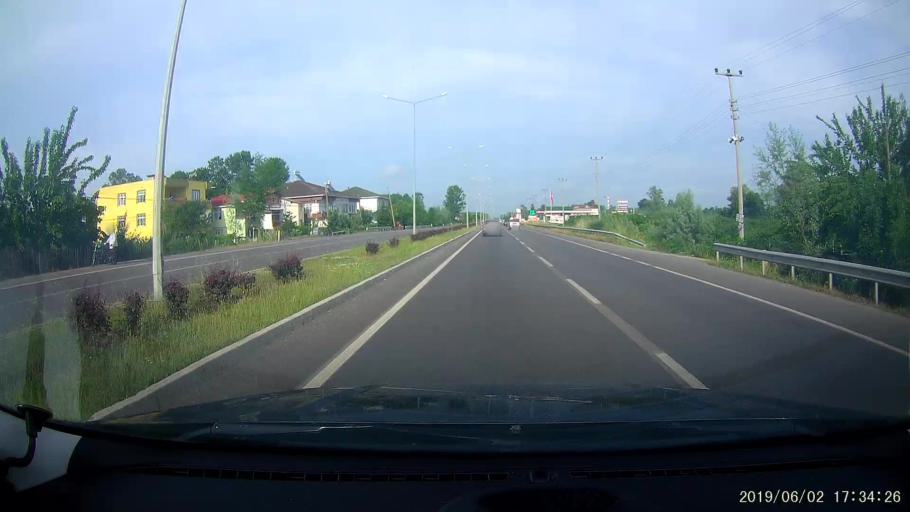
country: TR
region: Samsun
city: Terme
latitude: 41.2202
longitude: 36.8687
